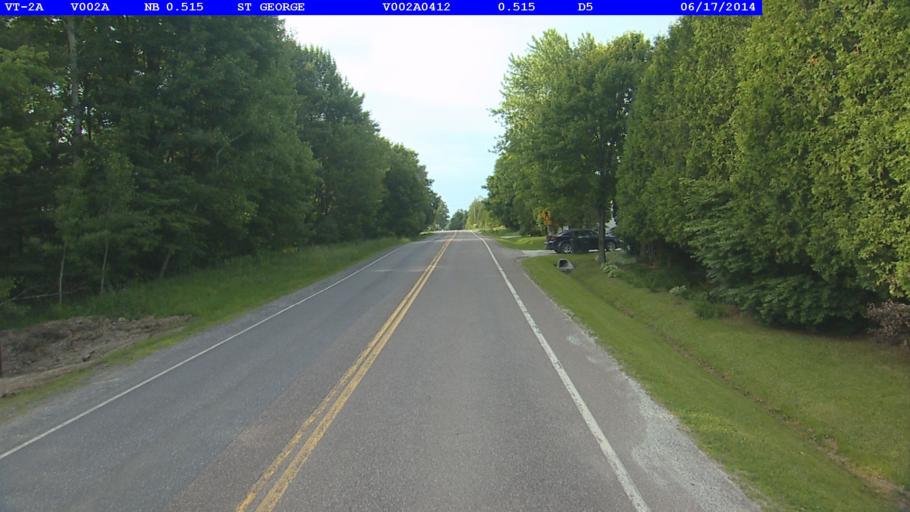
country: US
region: Vermont
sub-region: Chittenden County
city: Hinesburg
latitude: 44.3770
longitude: -73.1266
